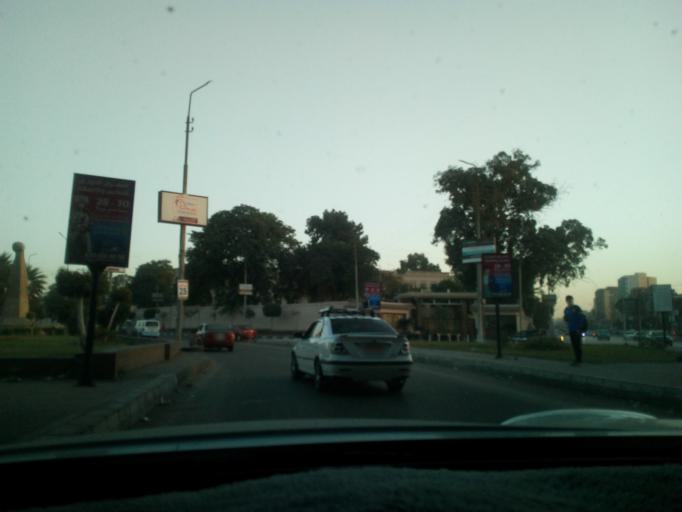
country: EG
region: Muhafazat al Qahirah
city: Cairo
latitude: 30.0953
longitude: 31.3426
